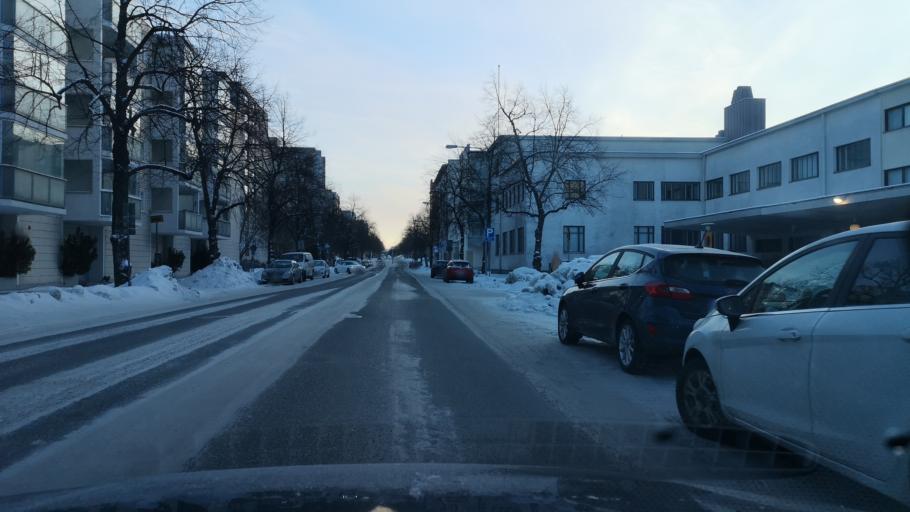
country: FI
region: Satakunta
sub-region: Pori
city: Pori
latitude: 61.4888
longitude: 21.7847
